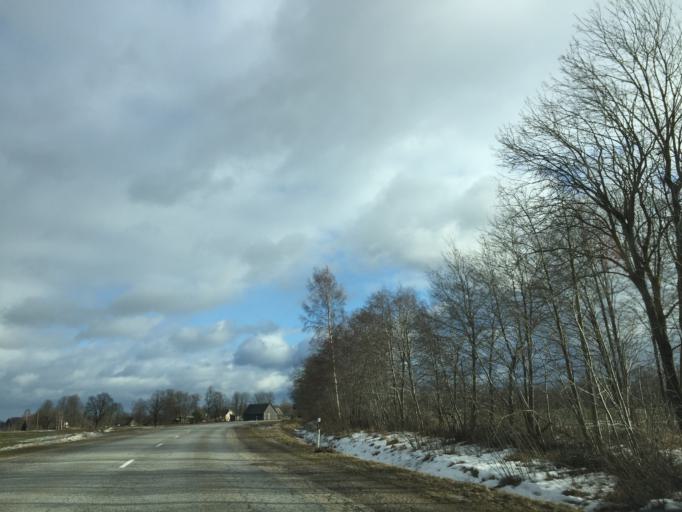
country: LV
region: Aloja
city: Staicele
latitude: 57.8946
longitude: 24.6343
